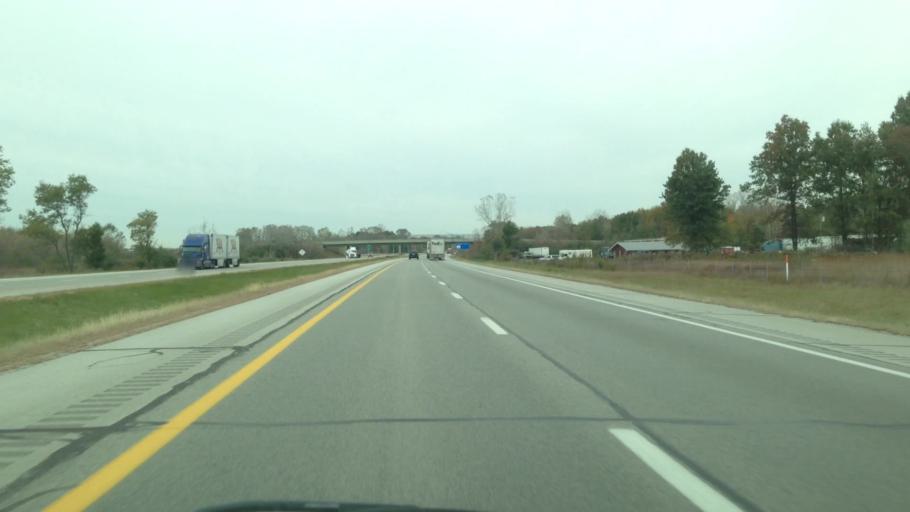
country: US
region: Ohio
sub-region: Lucas County
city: Holland
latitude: 41.5953
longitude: -83.7821
